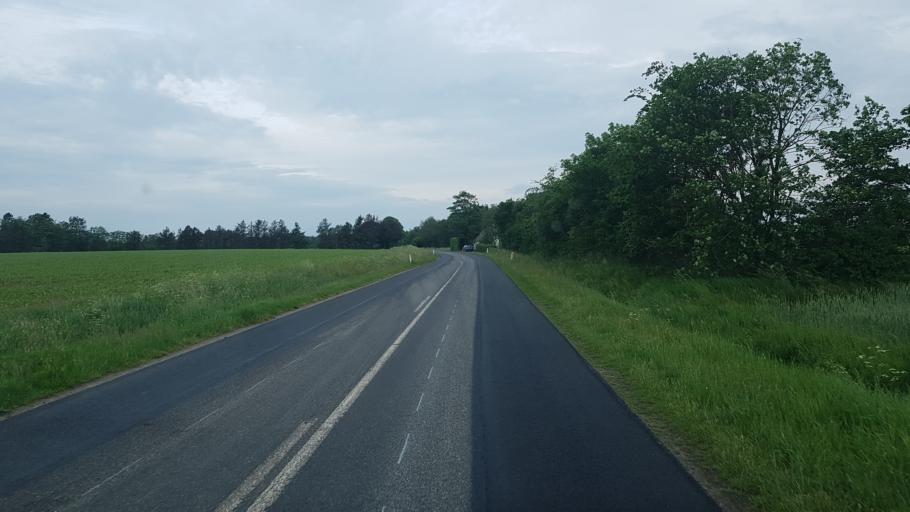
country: DK
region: South Denmark
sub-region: Vejen Kommune
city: Brorup
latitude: 55.4409
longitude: 8.9867
